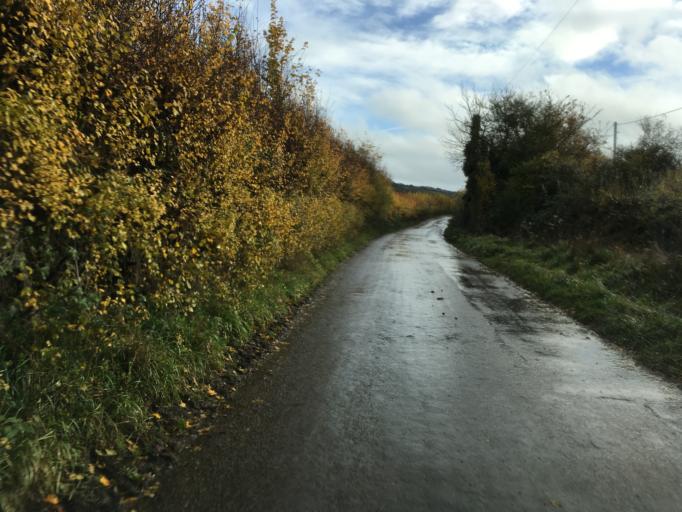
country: GB
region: England
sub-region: South Gloucestershire
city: Hinton
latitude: 51.4607
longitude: -2.4067
